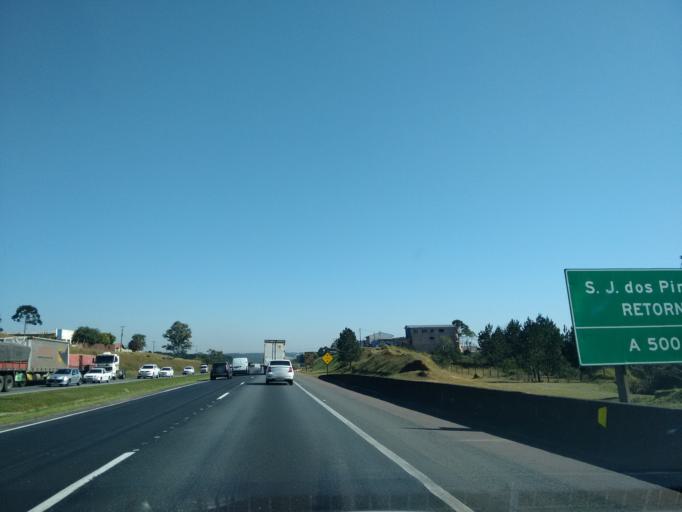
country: BR
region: Parana
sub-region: Sao Jose Dos Pinhais
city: Sao Jose dos Pinhais
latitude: -25.5707
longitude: -49.2133
